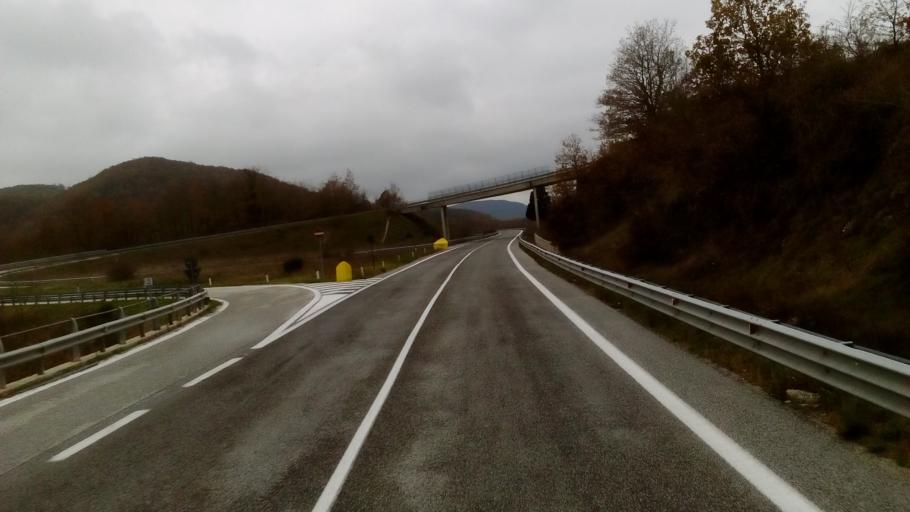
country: IT
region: Molise
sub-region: Provincia di Isernia
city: Chiauci
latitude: 41.6721
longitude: 14.3753
